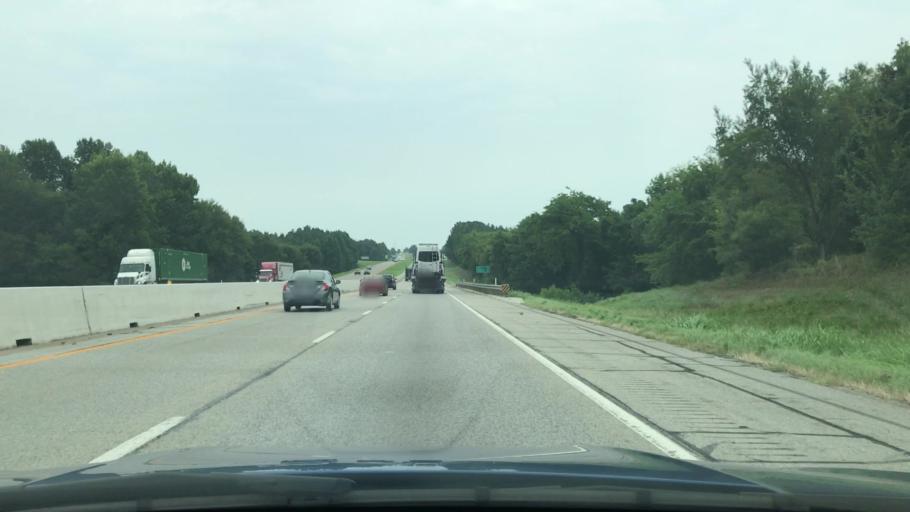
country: US
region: Texas
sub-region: Smith County
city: Hideaway
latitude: 32.4820
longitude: -95.5103
